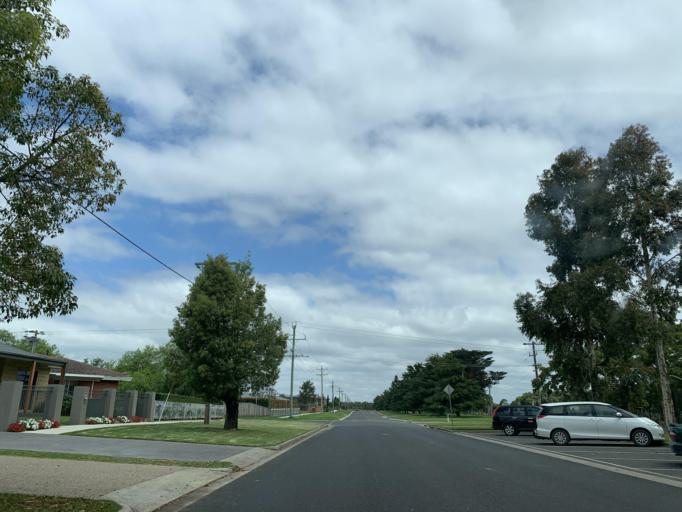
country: AU
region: Victoria
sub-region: Wellington
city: Sale
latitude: -38.1149
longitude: 147.0806
